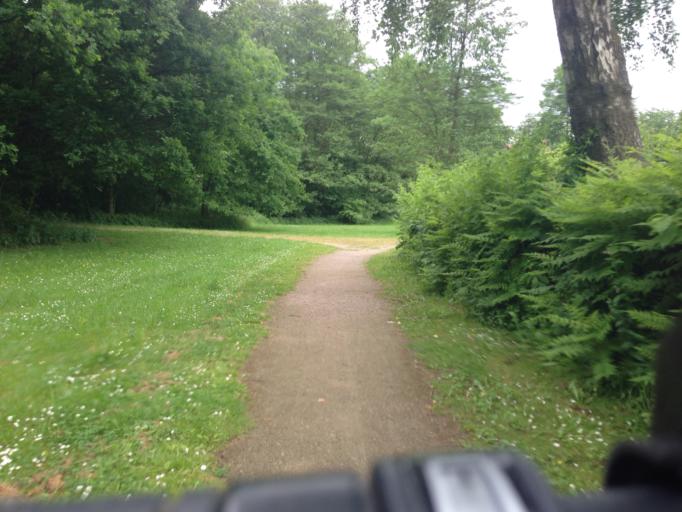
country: DE
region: Schleswig-Holstein
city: Barsbuettel
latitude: 53.5827
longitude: 10.1596
